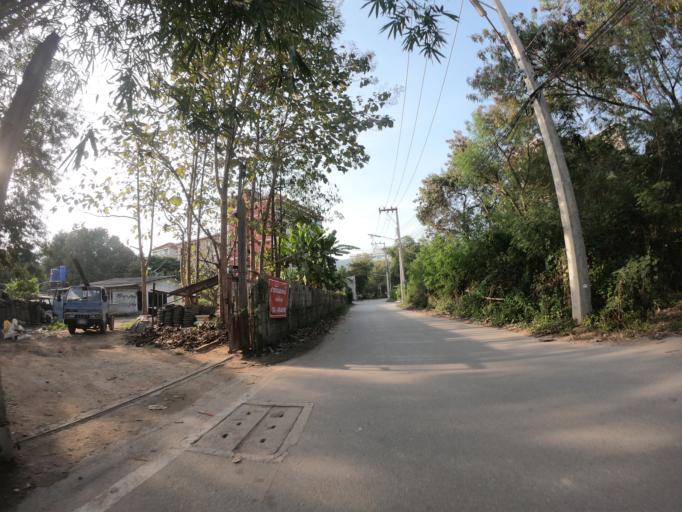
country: TH
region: Chiang Mai
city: Chiang Mai
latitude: 18.8219
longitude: 98.9636
